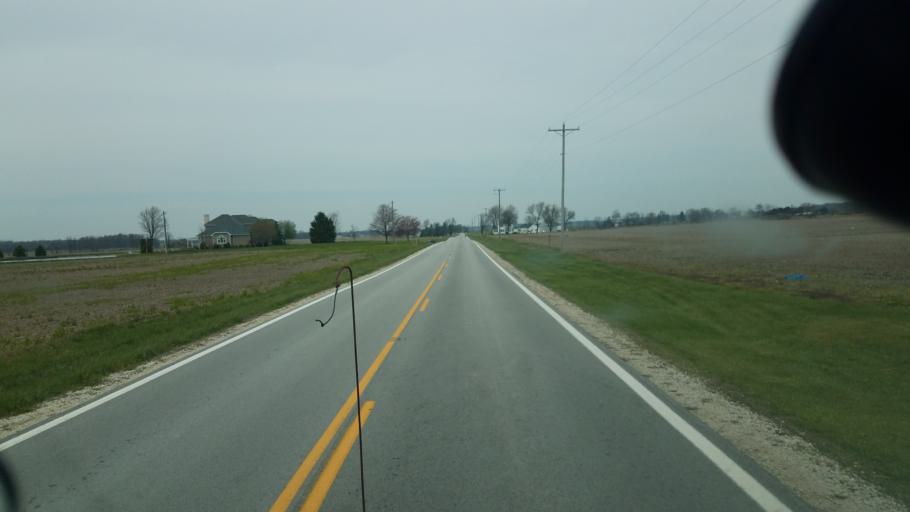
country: US
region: Ohio
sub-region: Wyandot County
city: Carey
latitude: 40.9776
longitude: -83.4767
